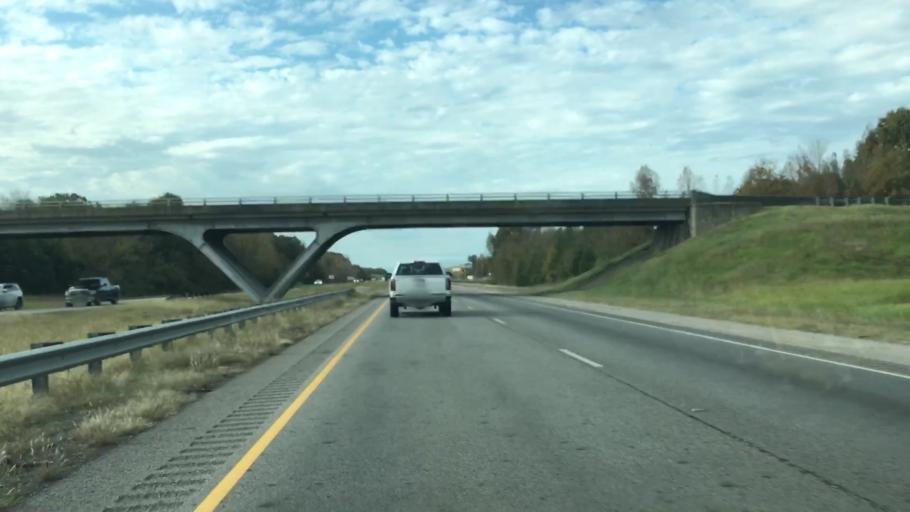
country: US
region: Arkansas
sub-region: Conway County
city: Morrilton
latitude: 35.2191
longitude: -92.8295
